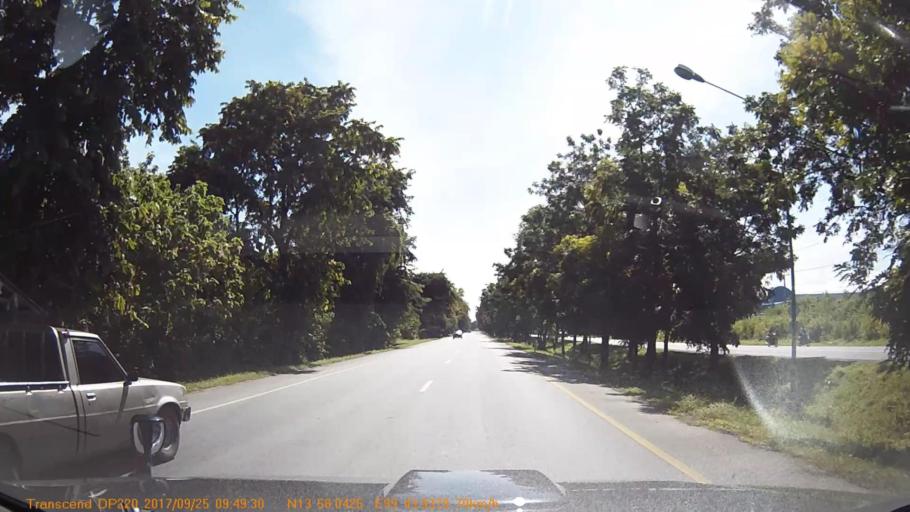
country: TH
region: Kanchanaburi
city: Tha Maka
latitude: 13.9673
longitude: 99.7327
